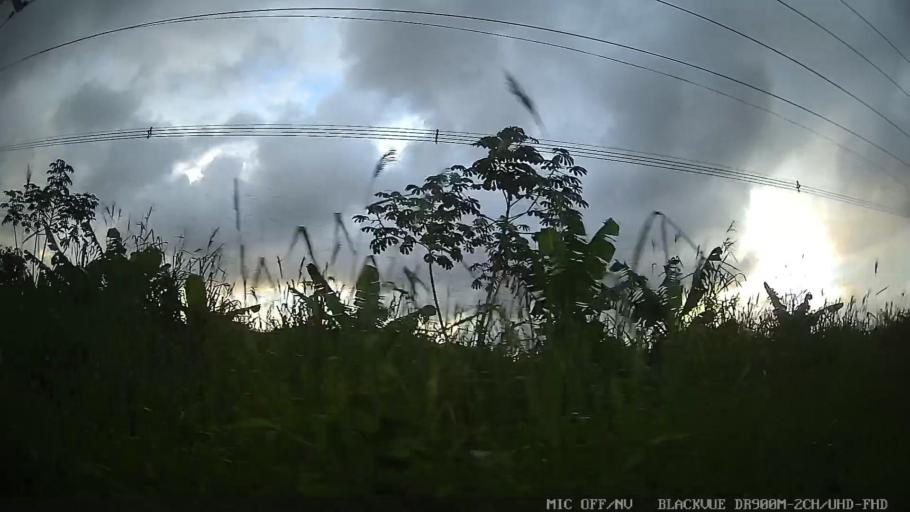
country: BR
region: Sao Paulo
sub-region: Itanhaem
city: Itanhaem
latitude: -24.0911
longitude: -46.7967
